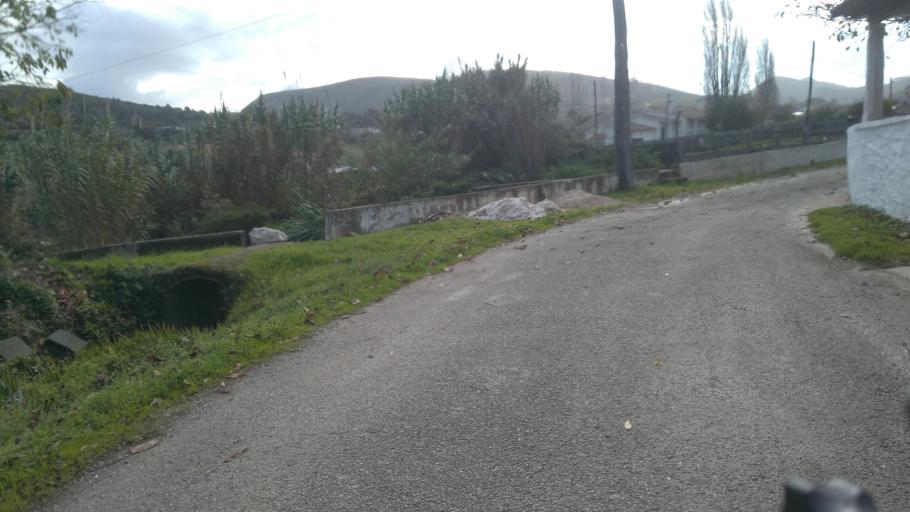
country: PT
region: Leiria
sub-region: Porto de Mos
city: Porto de Mos
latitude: 39.5903
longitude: -8.8187
